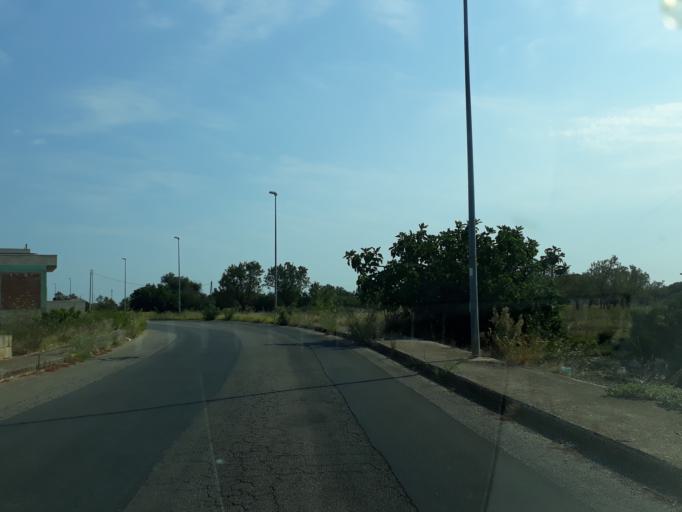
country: IT
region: Apulia
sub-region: Provincia di Brindisi
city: Carovigno
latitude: 40.6986
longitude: 17.6667
